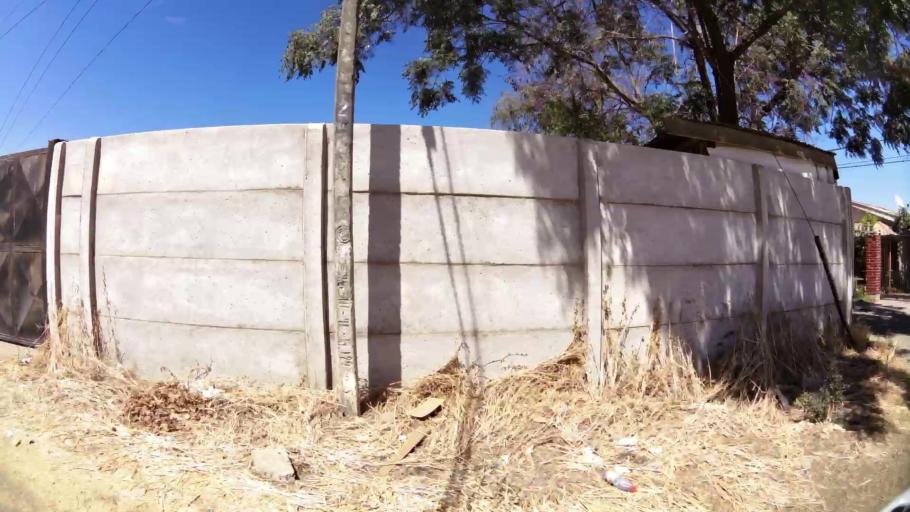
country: CL
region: O'Higgins
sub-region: Provincia de Cachapoal
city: Rancagua
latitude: -34.1614
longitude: -70.7515
